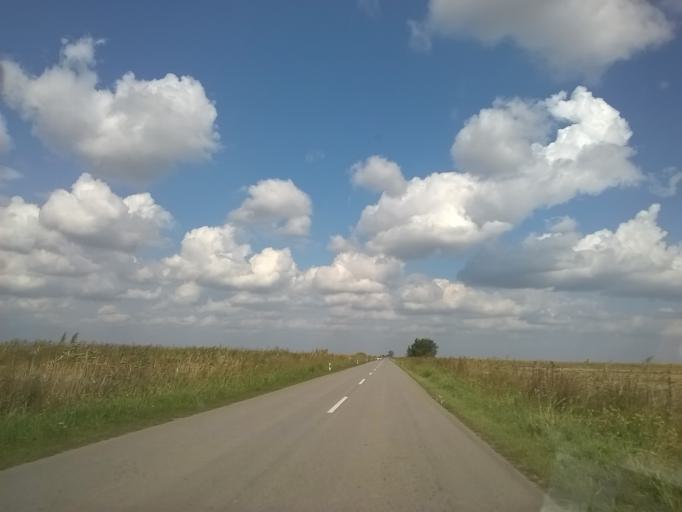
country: RS
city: Lokve
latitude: 45.1304
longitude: 21.0318
